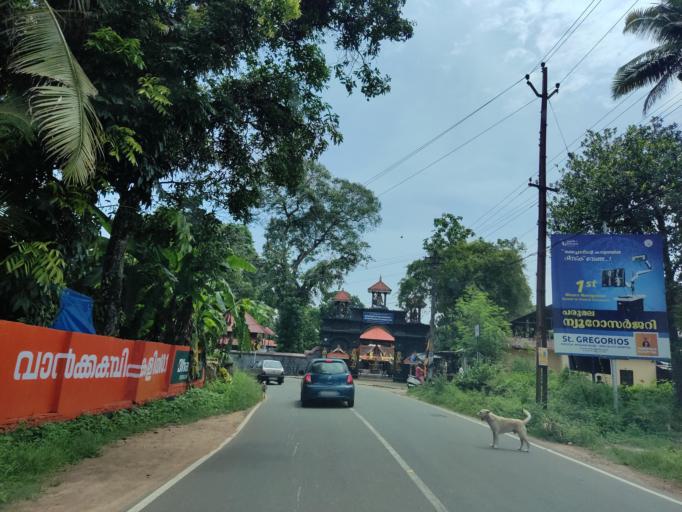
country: IN
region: Kerala
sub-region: Alappuzha
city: Chengannur
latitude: 9.3115
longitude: 76.6034
